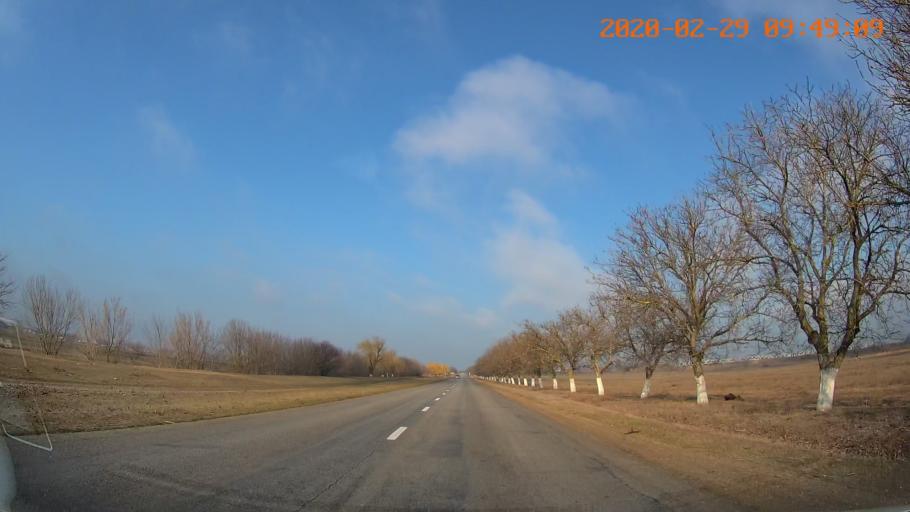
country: MD
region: Telenesti
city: Crasnoe
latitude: 46.6953
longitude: 29.7764
